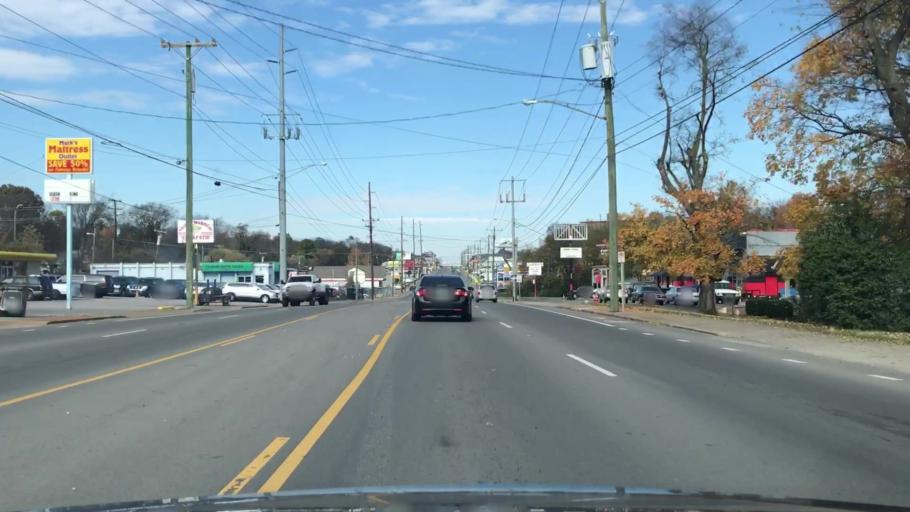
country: US
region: Tennessee
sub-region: Davidson County
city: Oak Hill
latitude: 36.0964
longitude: -86.7378
